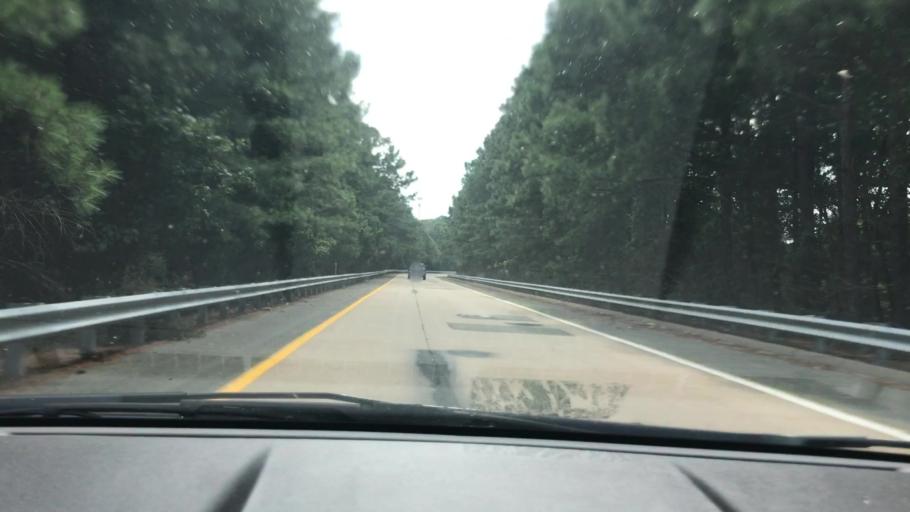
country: US
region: Virginia
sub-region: Henrico County
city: Short Pump
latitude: 37.6714
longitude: -77.5851
